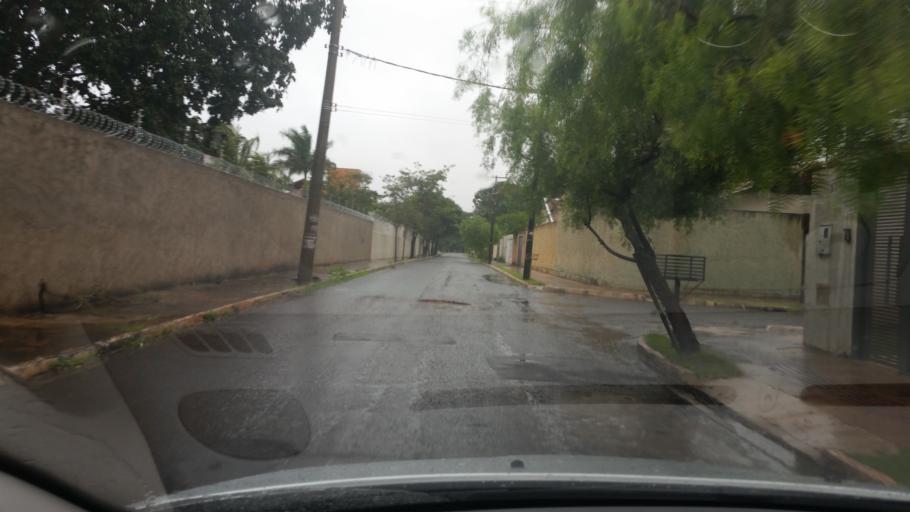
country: BR
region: Mato Grosso do Sul
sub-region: Campo Grande
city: Campo Grande
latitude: -20.4584
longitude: -54.5664
